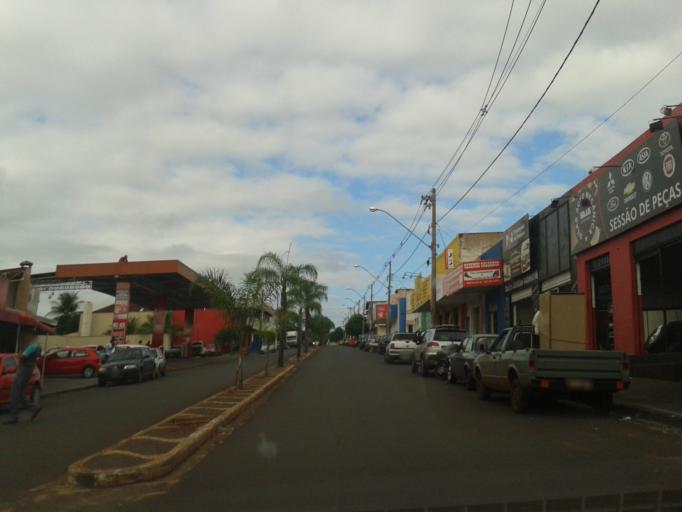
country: BR
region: Minas Gerais
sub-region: Ituiutaba
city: Ituiutaba
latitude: -18.9771
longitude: -49.4733
